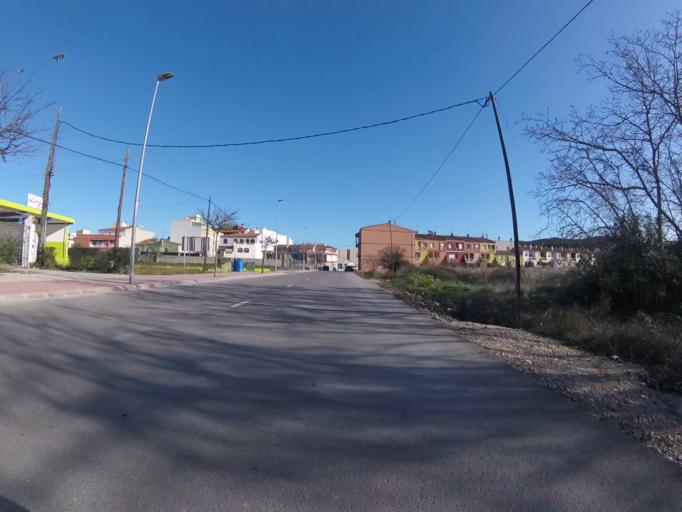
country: ES
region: Valencia
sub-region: Provincia de Castello
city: Alcala de Xivert
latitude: 40.3002
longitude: 0.2237
